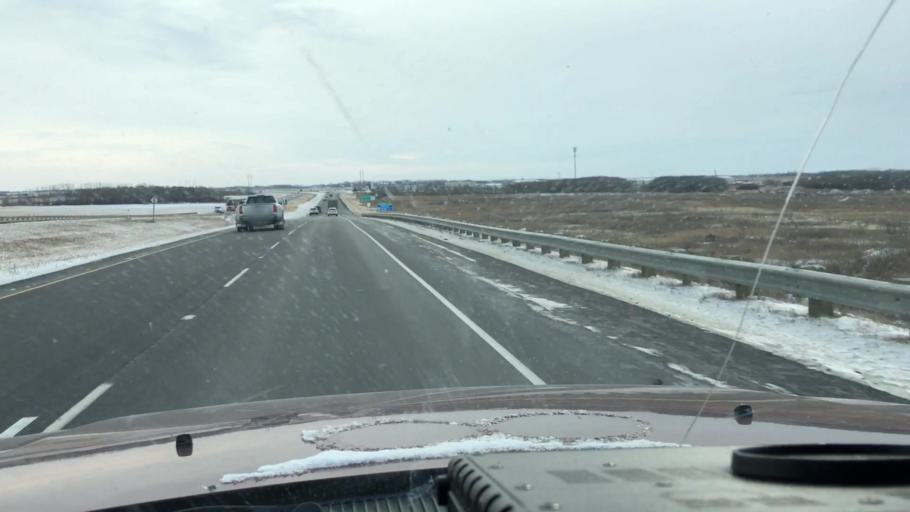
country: CA
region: Saskatchewan
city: Saskatoon
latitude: 52.0685
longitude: -106.6031
